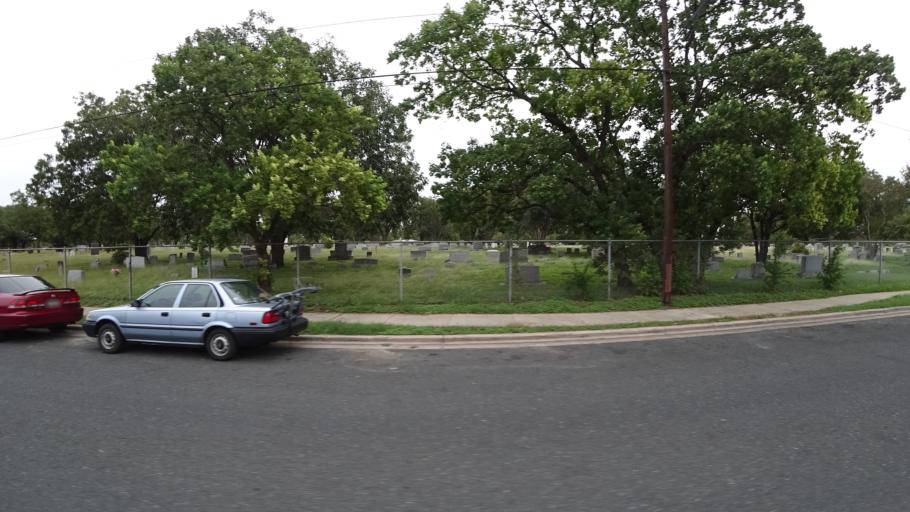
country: US
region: Texas
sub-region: Travis County
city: Austin
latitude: 30.2777
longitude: -97.7248
